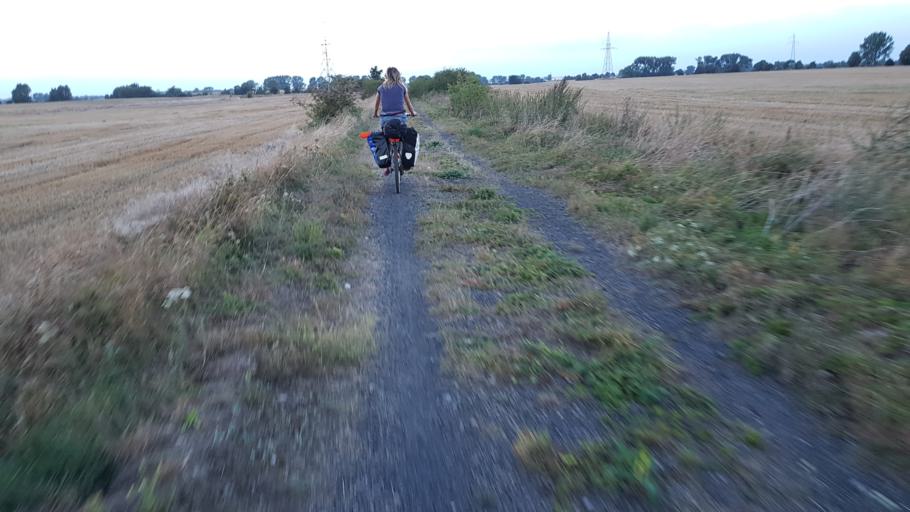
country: PL
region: West Pomeranian Voivodeship
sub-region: Powiat pyrzycki
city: Przelewice
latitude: 53.1293
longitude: 15.0431
